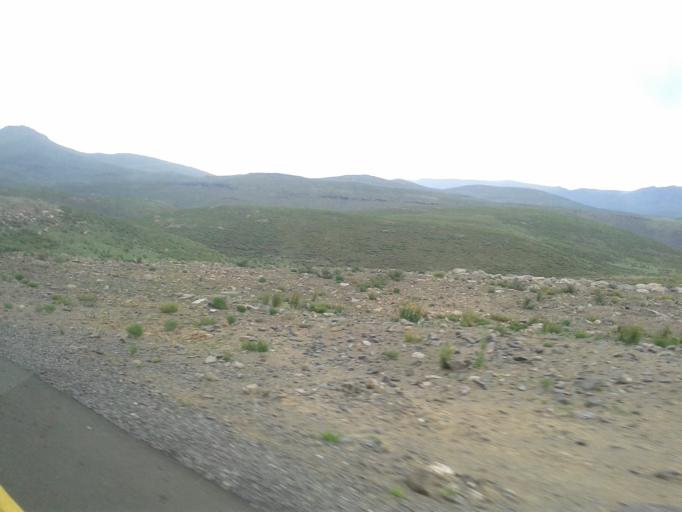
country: LS
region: Maseru
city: Nako
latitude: -29.7554
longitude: 27.9786
